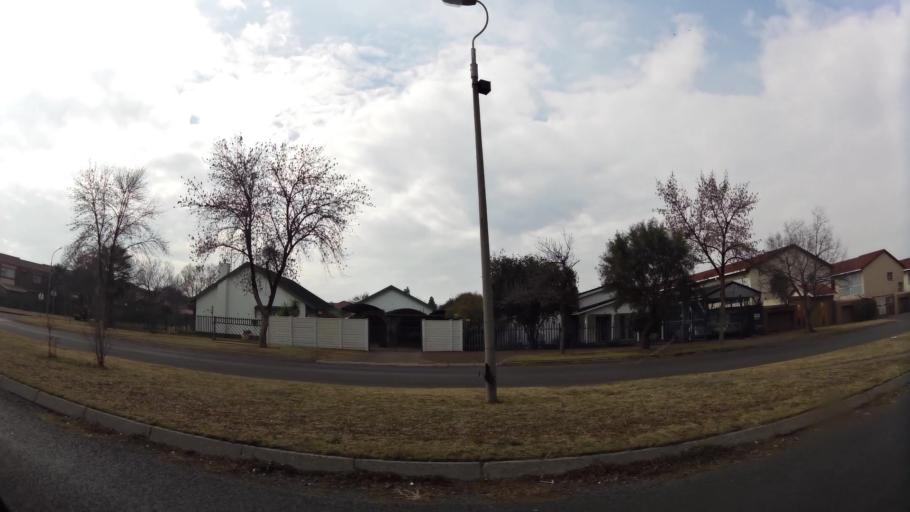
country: ZA
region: Gauteng
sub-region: Sedibeng District Municipality
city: Vanderbijlpark
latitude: -26.6950
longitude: 27.8474
